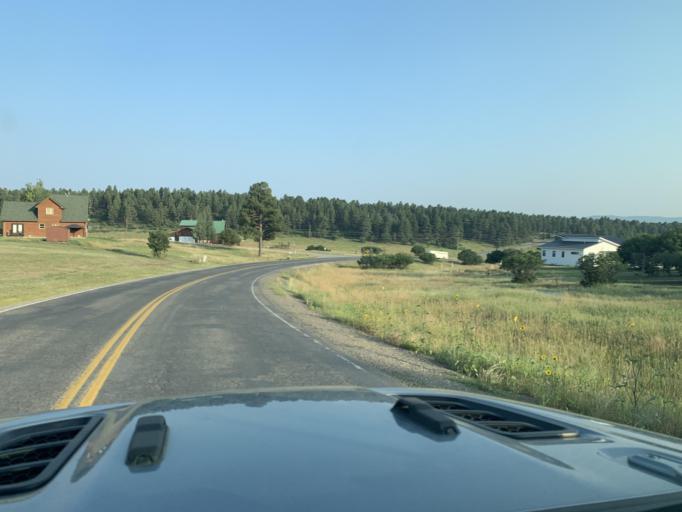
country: US
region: Colorado
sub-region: Archuleta County
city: Pagosa Springs
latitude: 37.2872
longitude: -107.0962
